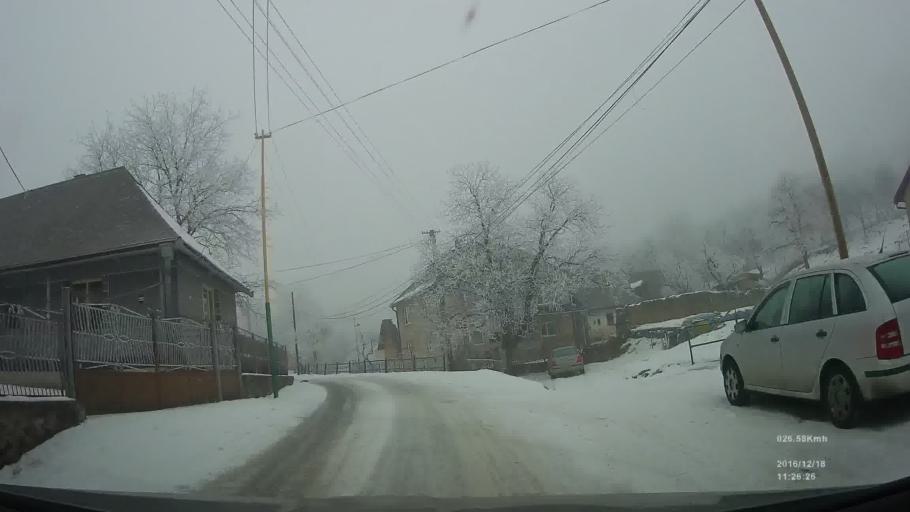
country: SK
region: Presovsky
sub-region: Okres Presov
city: Presov
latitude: 48.9002
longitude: 21.4077
